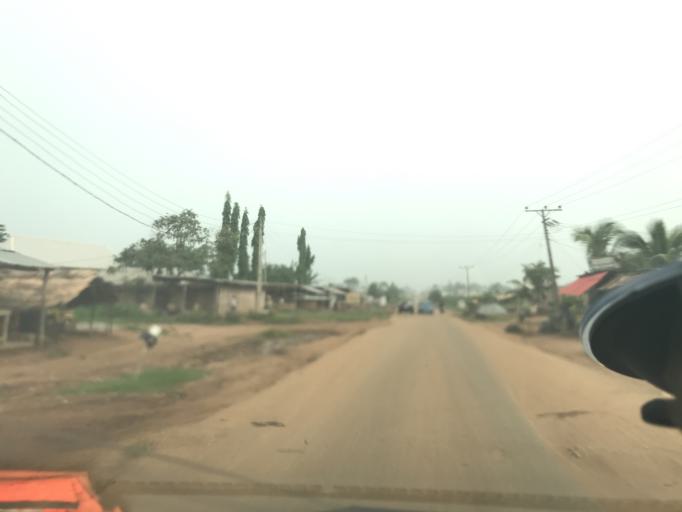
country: NG
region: Ogun
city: Ado Odo
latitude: 6.5153
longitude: 2.9536
